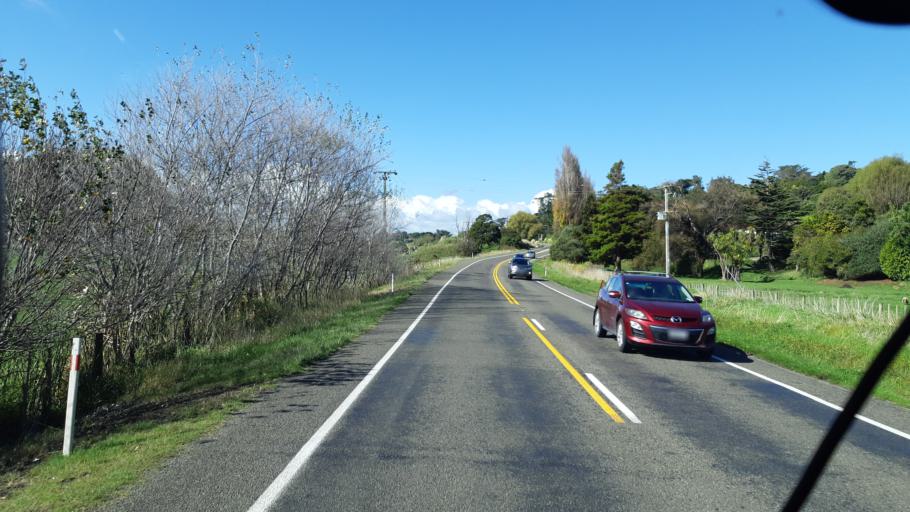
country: NZ
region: Manawatu-Wanganui
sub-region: Wanganui District
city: Wanganui
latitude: -39.9535
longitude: 175.0631
